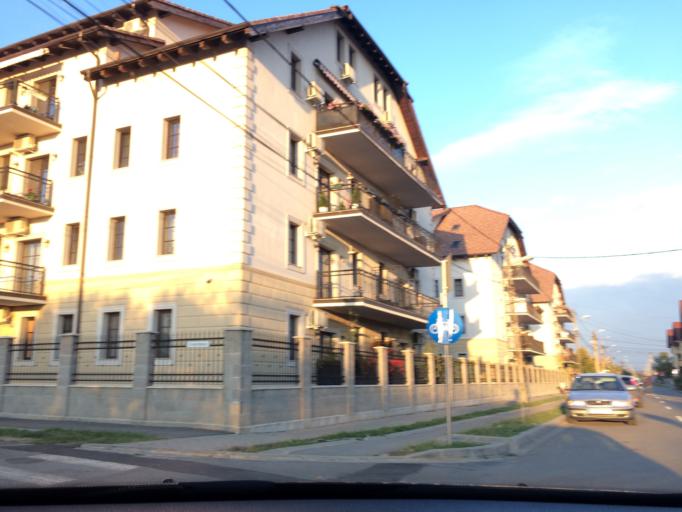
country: RO
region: Timis
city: Timisoara
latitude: 45.7602
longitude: 21.1834
